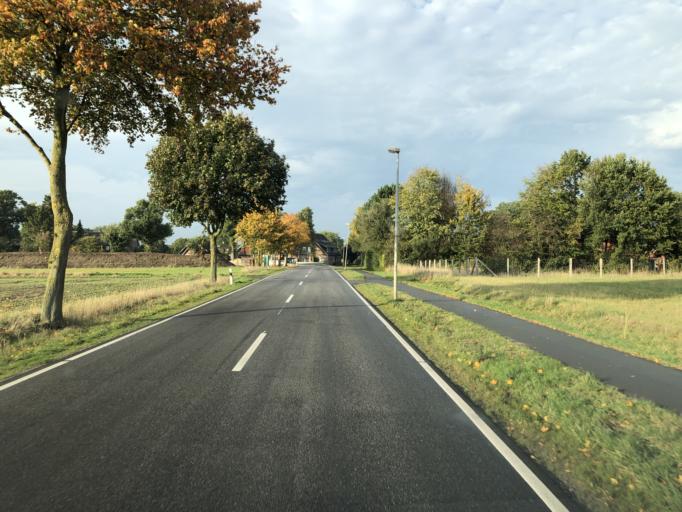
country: DE
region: Lower Saxony
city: Neu Wulmstorf
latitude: 53.4409
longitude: 9.8055
